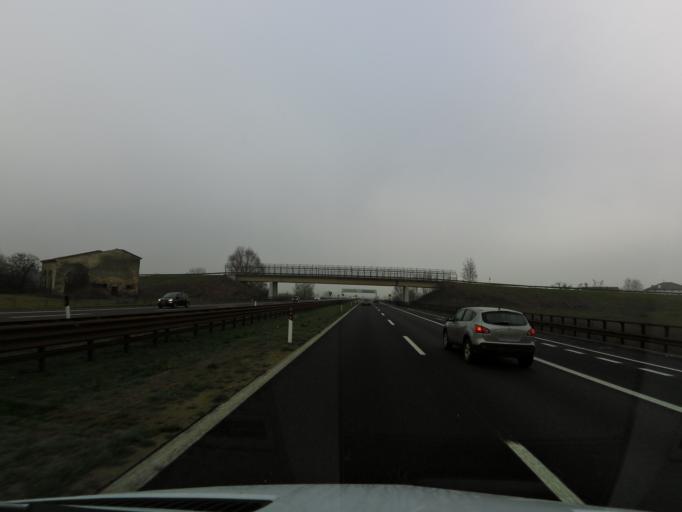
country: IT
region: Lombardy
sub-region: Provincia di Mantova
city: Pegognaga
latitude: 45.0294
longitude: 10.8539
